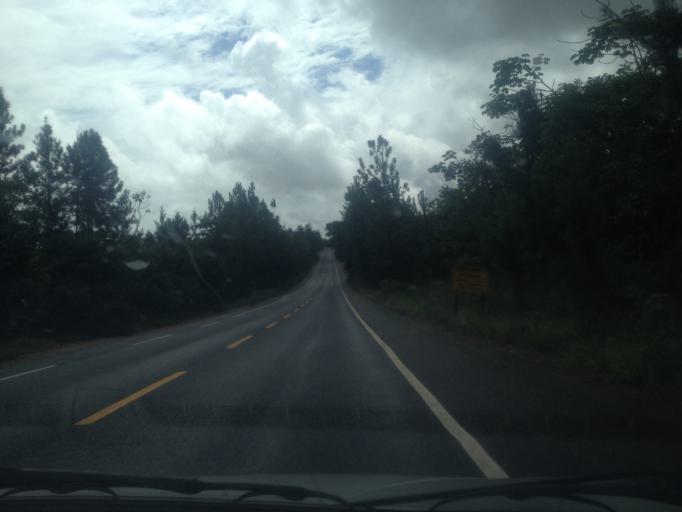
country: BR
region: Bahia
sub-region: Entre Rios
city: Entre Rios
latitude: -12.1104
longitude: -37.7851
